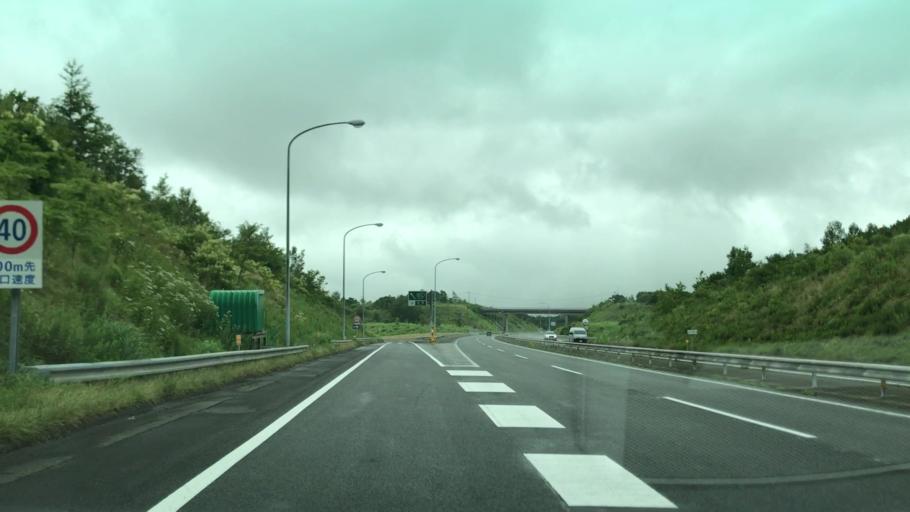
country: JP
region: Hokkaido
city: Muroran
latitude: 42.3864
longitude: 140.9743
